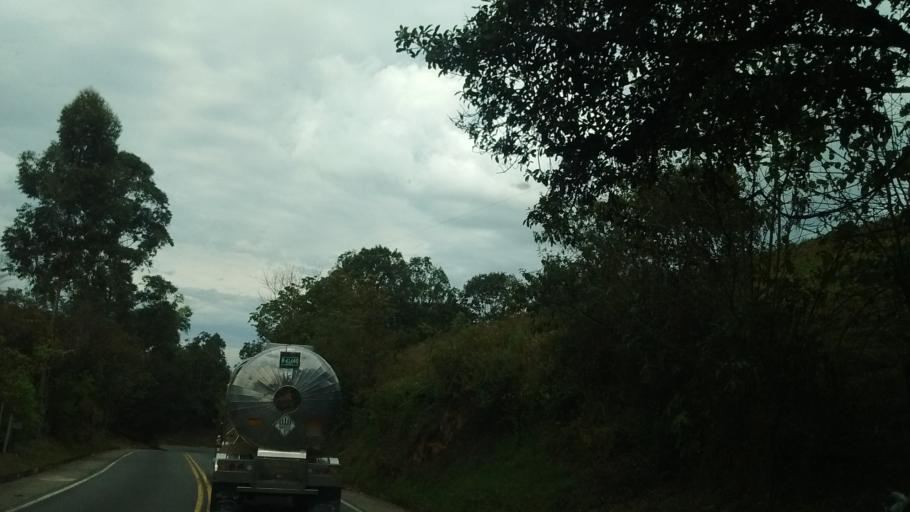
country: CO
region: Cauca
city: Rosas
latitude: 2.3101
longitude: -76.6899
